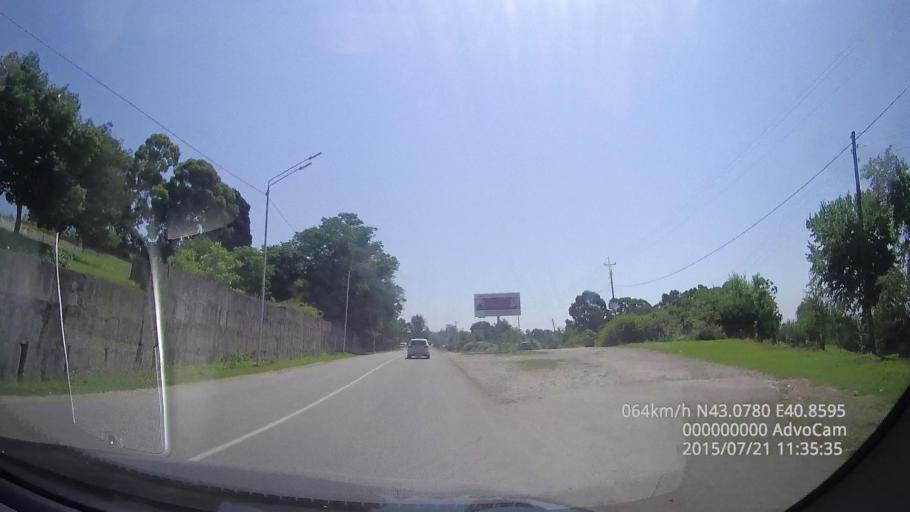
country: GE
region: Abkhazia
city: Stantsiya Novyy Afon
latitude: 43.0778
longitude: 40.8601
